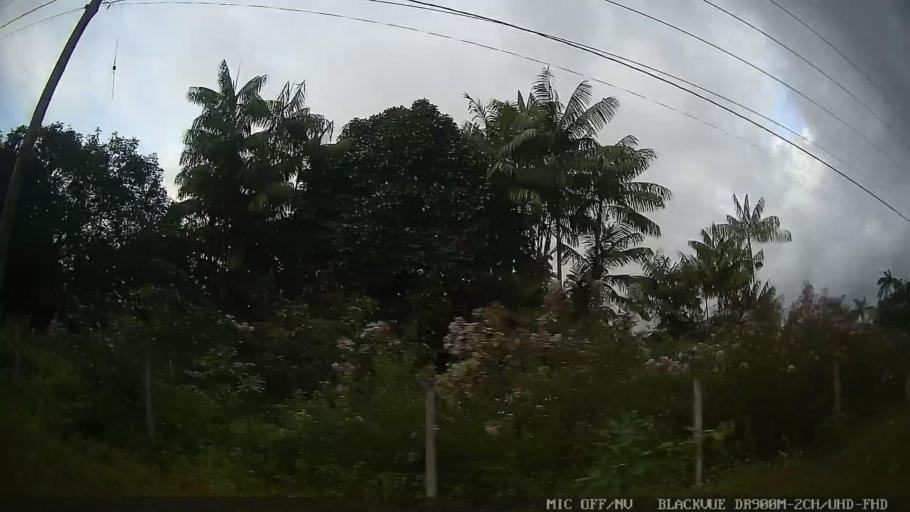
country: BR
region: Sao Paulo
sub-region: Itanhaem
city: Itanhaem
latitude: -24.0877
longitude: -46.7973
